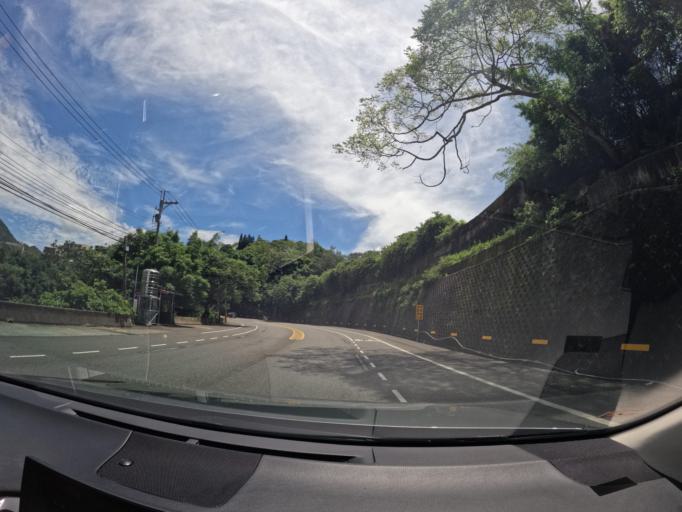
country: TW
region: Taiwan
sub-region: Miaoli
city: Miaoli
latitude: 24.4867
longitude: 120.9000
